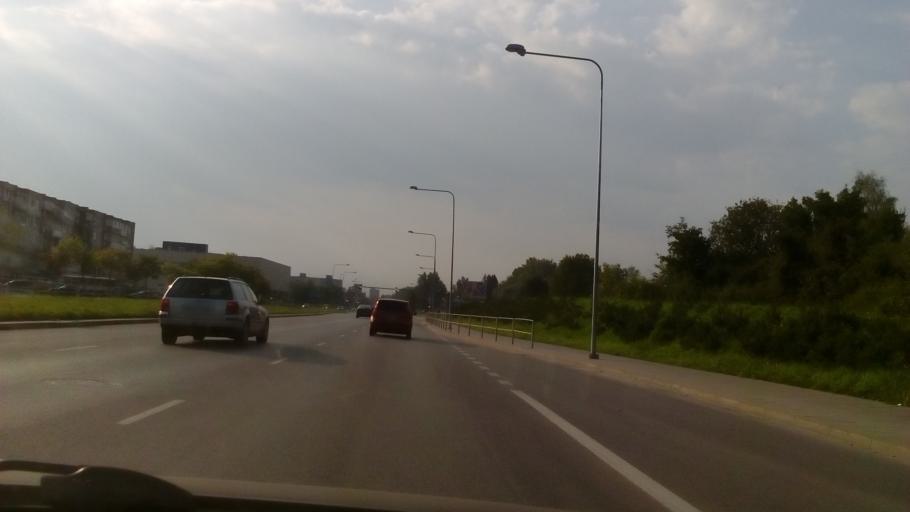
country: LT
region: Alytaus apskritis
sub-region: Alytus
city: Alytus
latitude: 54.4065
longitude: 24.0186
